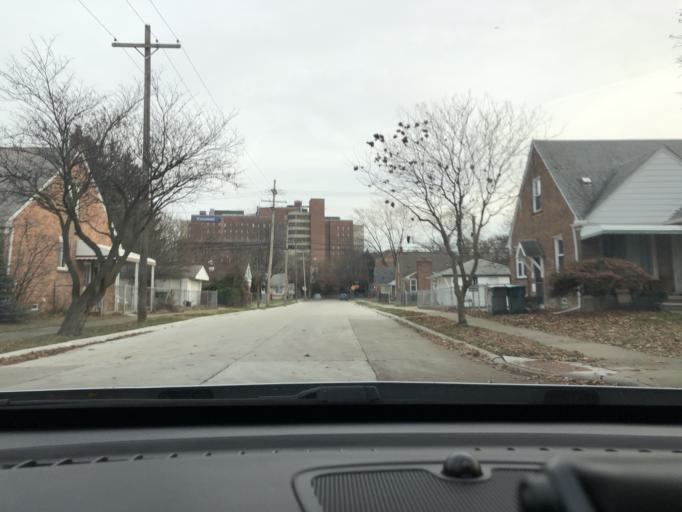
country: US
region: Michigan
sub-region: Wayne County
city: Allen Park
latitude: 42.2919
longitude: -83.2171
